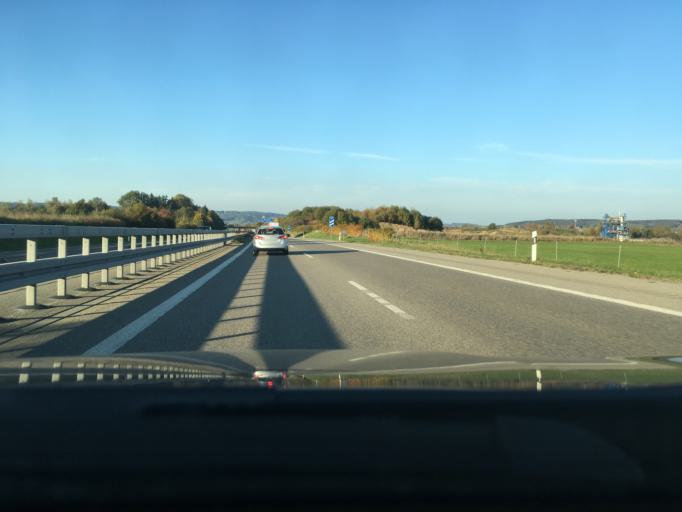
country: DE
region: Baden-Wuerttemberg
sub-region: Tuebingen Region
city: Leutkirch im Allgau
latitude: 47.8106
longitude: 9.9902
